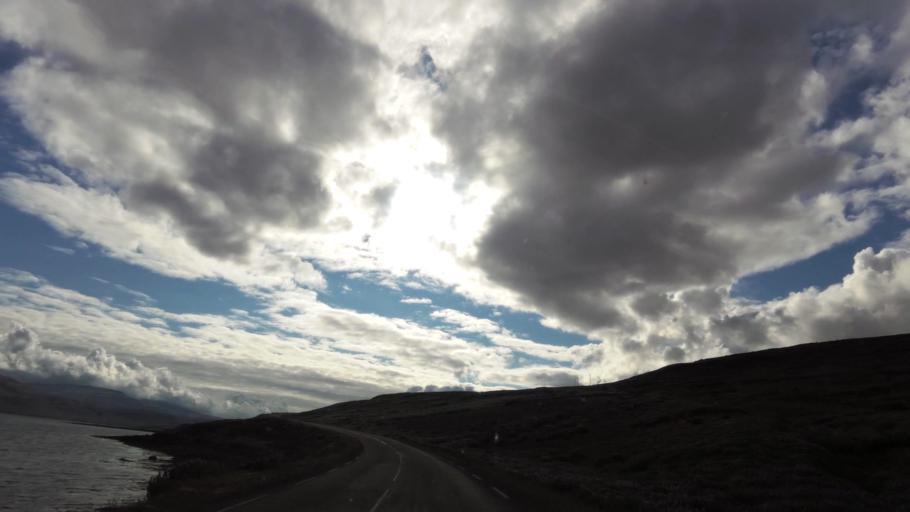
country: IS
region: West
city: Olafsvik
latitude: 65.5389
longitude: -23.7975
